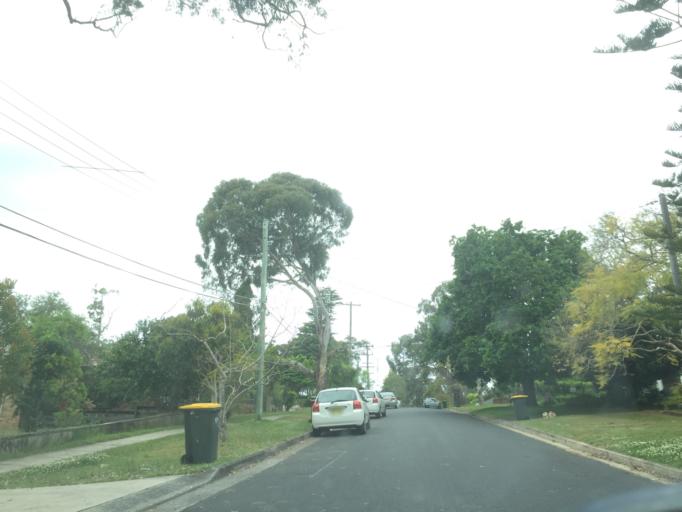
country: AU
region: New South Wales
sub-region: Willoughby
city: Lane Cove North
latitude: -33.8029
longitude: 151.1579
